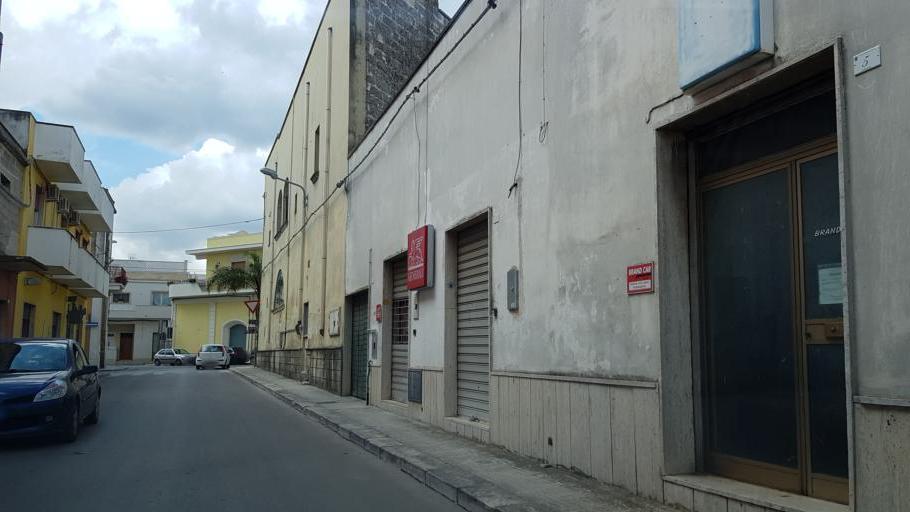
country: IT
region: Apulia
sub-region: Provincia di Brindisi
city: San Pancrazio Salentino
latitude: 40.4184
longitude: 17.8406
